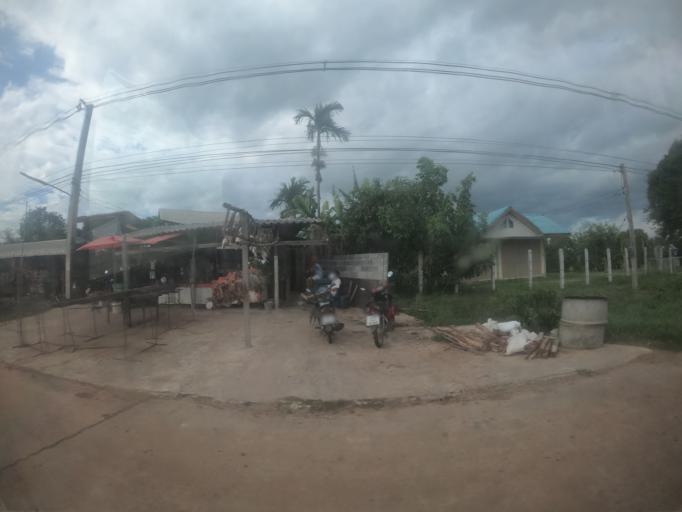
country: TH
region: Surin
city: Kap Choeng
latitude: 14.5469
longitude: 103.5136
